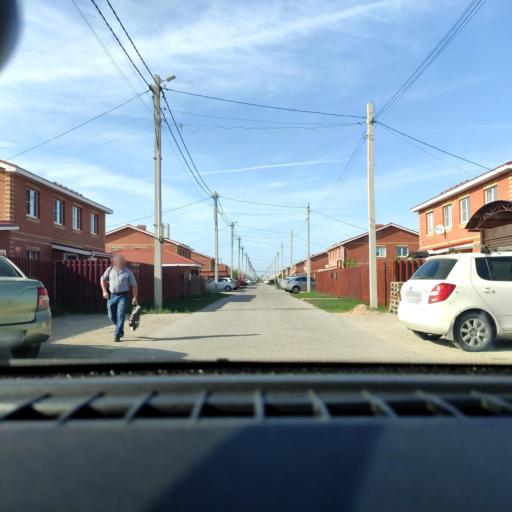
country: RU
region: Samara
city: Podstepki
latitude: 53.5745
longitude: 49.0838
